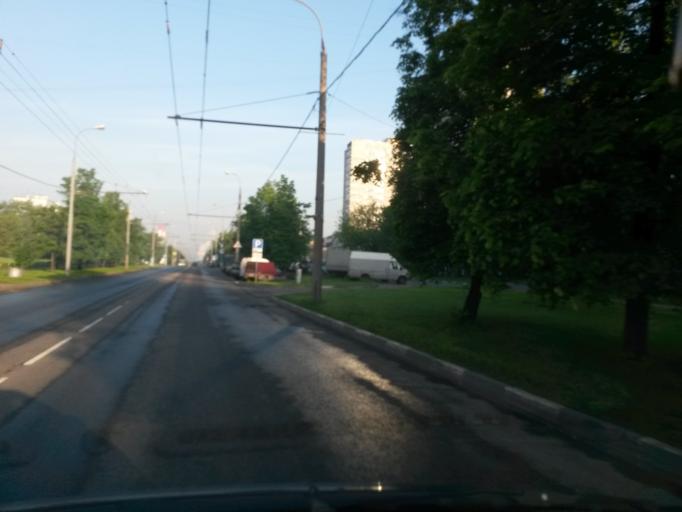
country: RU
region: Moscow
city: Gol'yanovo
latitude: 55.8236
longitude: 37.8210
